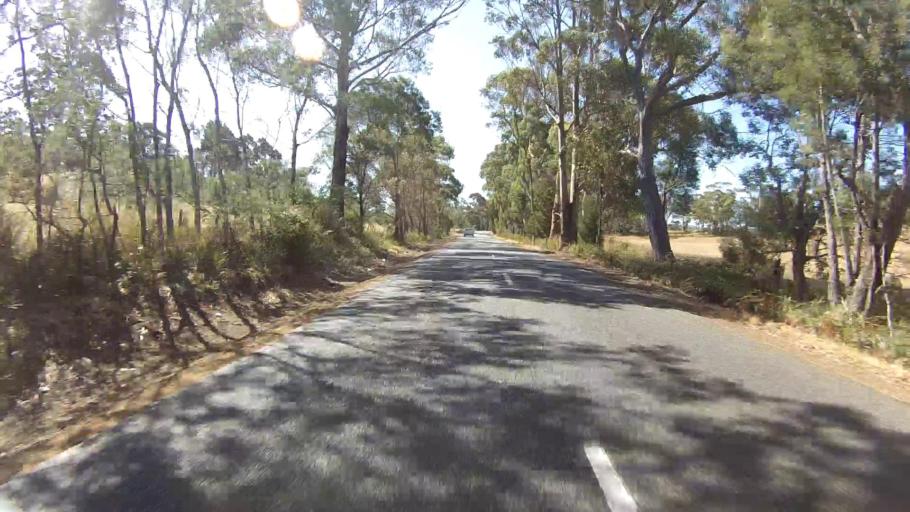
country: AU
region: Tasmania
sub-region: Sorell
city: Sorell
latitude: -42.3134
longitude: 147.9609
